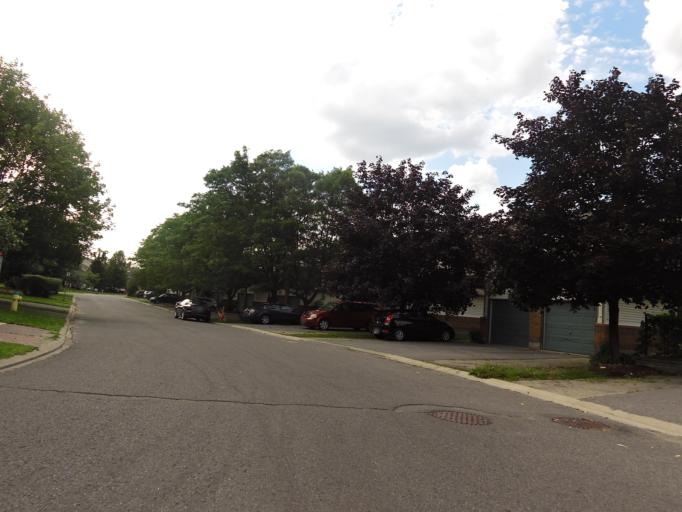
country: CA
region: Ontario
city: Bells Corners
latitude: 45.3465
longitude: -75.7668
